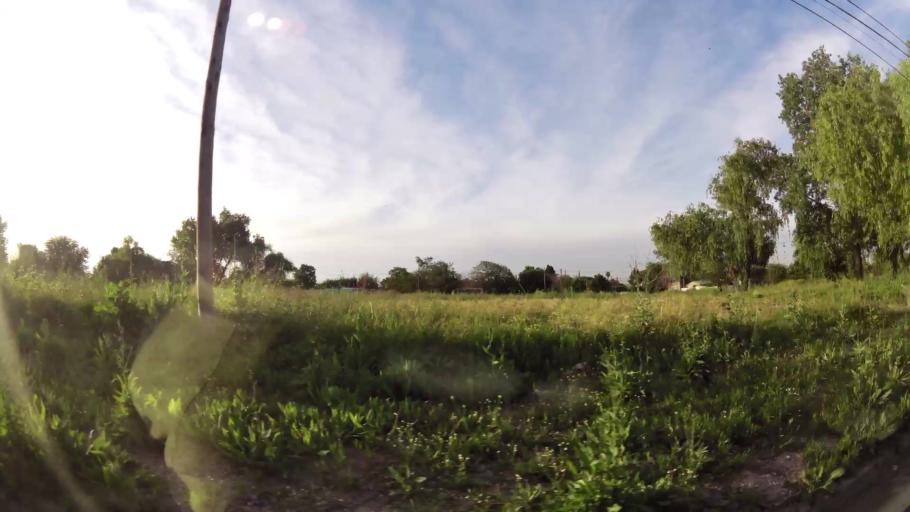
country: AR
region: Buenos Aires
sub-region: Partido de Almirante Brown
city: Adrogue
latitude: -34.7920
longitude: -58.3468
